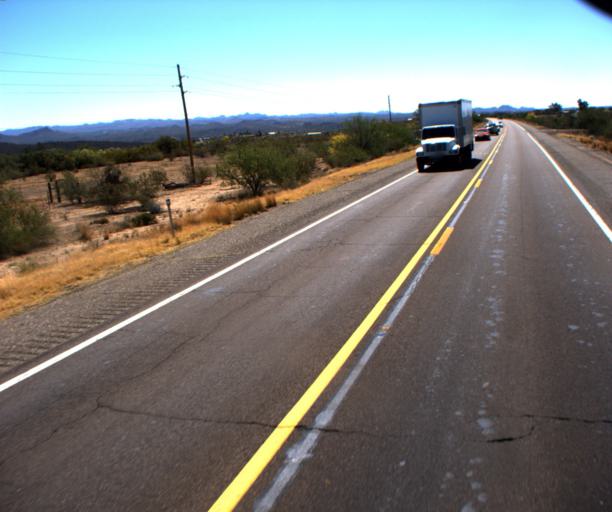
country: US
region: Arizona
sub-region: Maricopa County
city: Wickenburg
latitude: 34.0146
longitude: -112.7944
